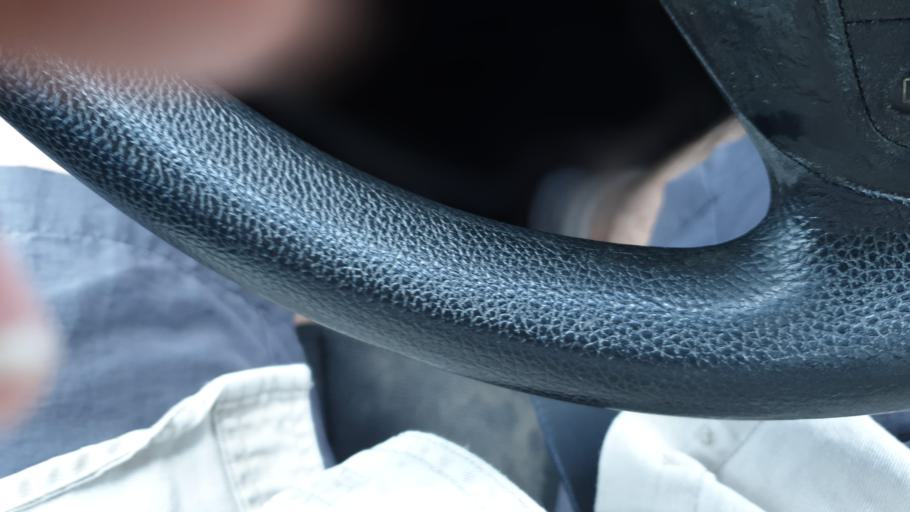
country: BE
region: Flanders
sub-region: Provincie West-Vlaanderen
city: Veurne
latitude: 51.0579
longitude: 2.6888
